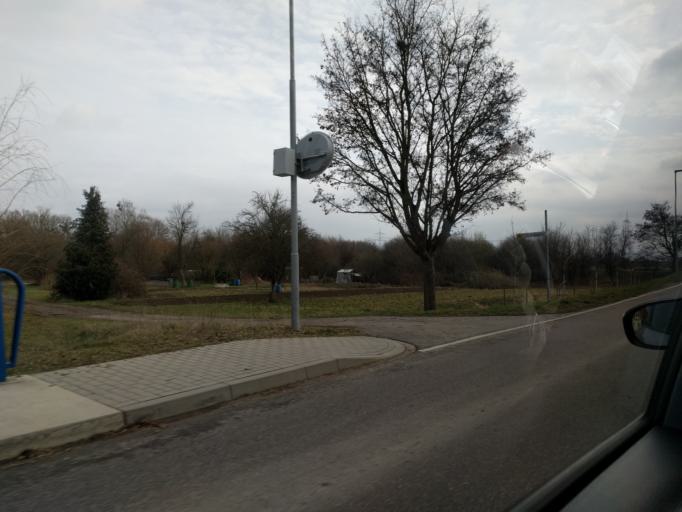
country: DE
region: Rheinland-Pfalz
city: Neuburg
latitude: 48.9687
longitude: 8.2696
